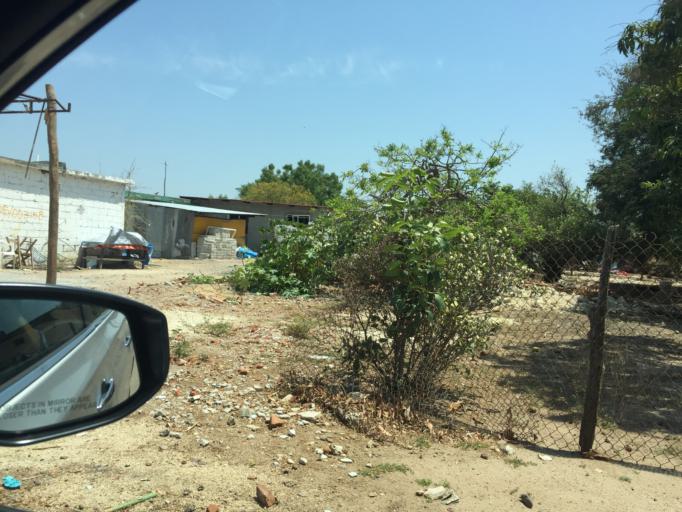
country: MX
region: Oaxaca
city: Asuncion Ixtaltepec
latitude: 16.5027
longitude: -95.0639
